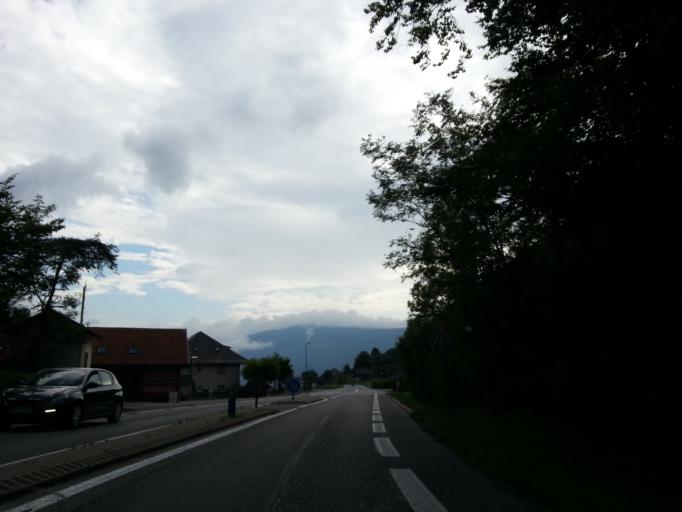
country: FR
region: Rhone-Alpes
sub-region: Departement de la Haute-Savoie
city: Menthon-Saint-Bernard
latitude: 45.8739
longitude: 6.2132
